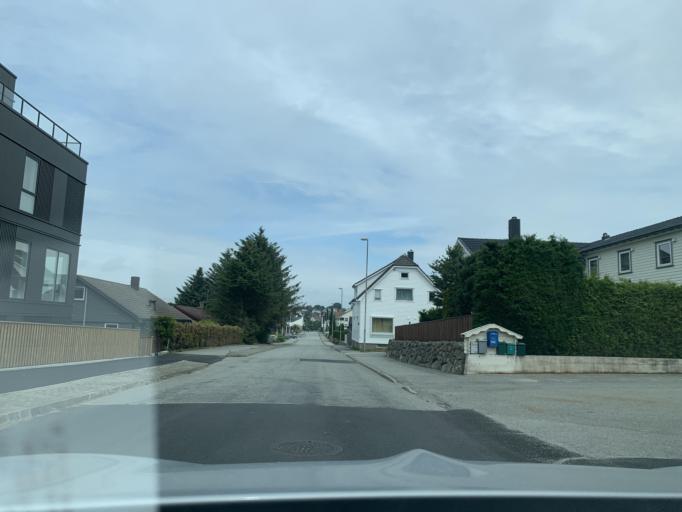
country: NO
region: Rogaland
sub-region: Time
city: Bryne
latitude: 58.7332
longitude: 5.6386
